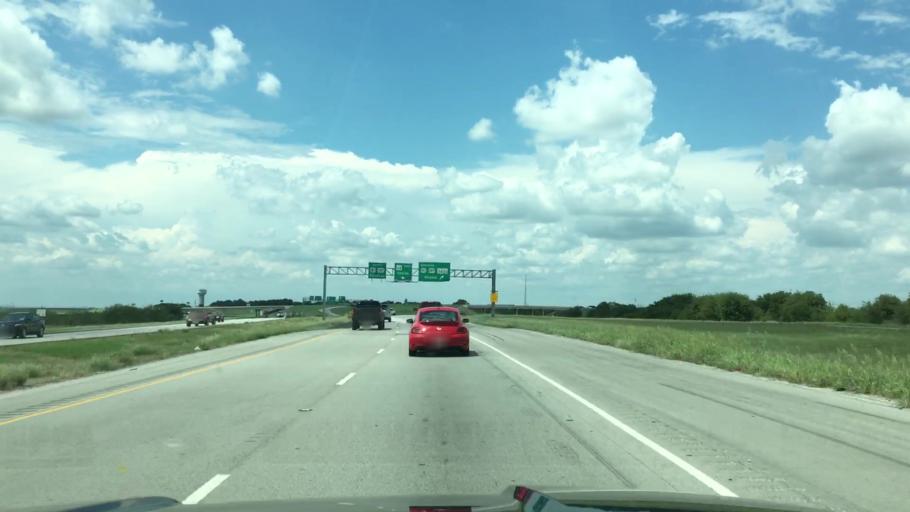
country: US
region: Texas
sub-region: Wise County
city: Rhome
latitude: 33.0412
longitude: -97.4572
